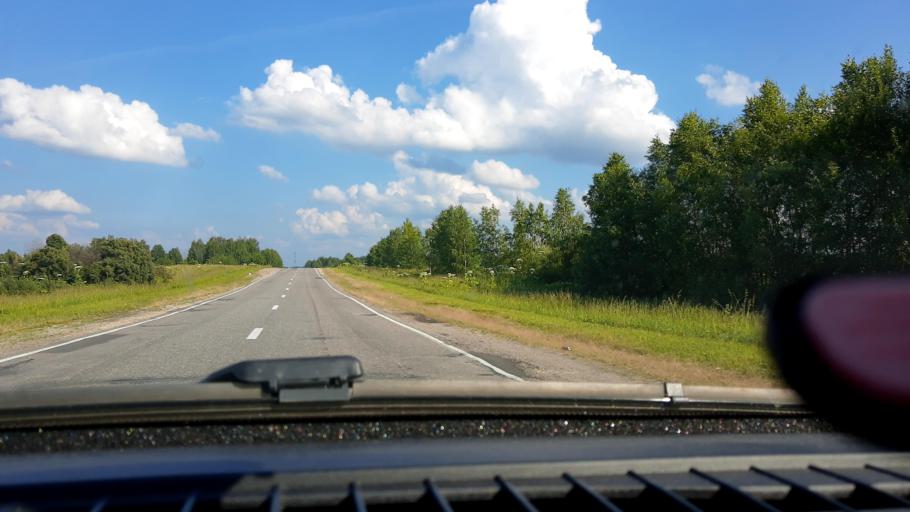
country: RU
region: Nizjnij Novgorod
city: Sitniki
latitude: 56.5000
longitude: 43.9927
